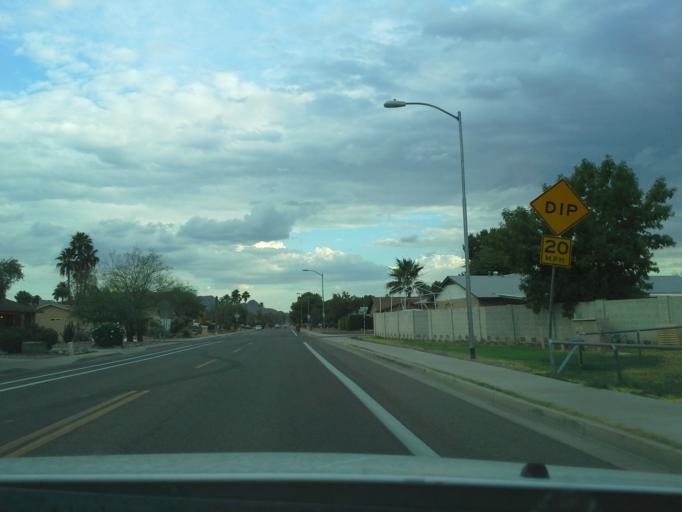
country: US
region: Arizona
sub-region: Maricopa County
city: Paradise Valley
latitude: 33.6028
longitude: -112.0046
